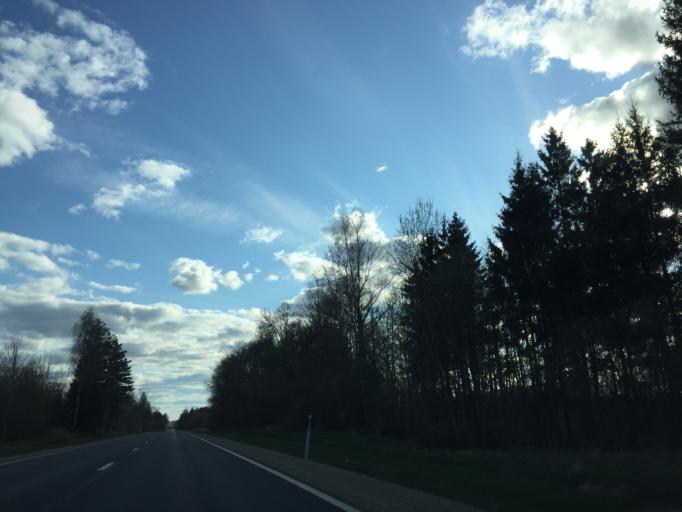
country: LV
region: Karsava
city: Karsava
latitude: 56.6624
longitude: 27.5146
